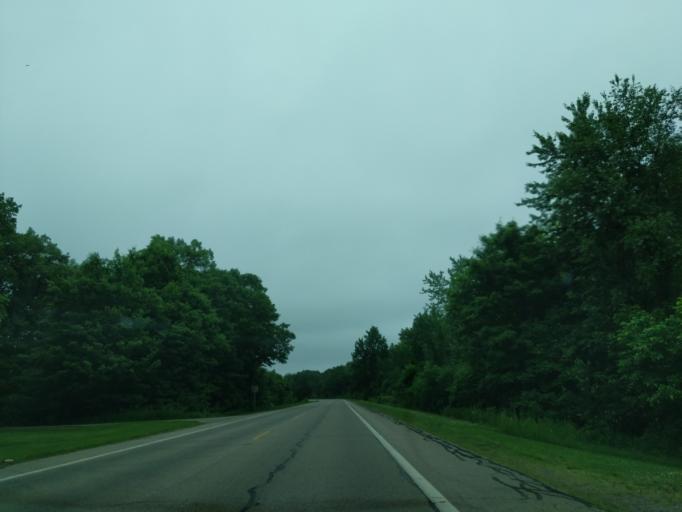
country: US
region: Michigan
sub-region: Hillsdale County
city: Litchfield
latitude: 42.0330
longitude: -84.7340
